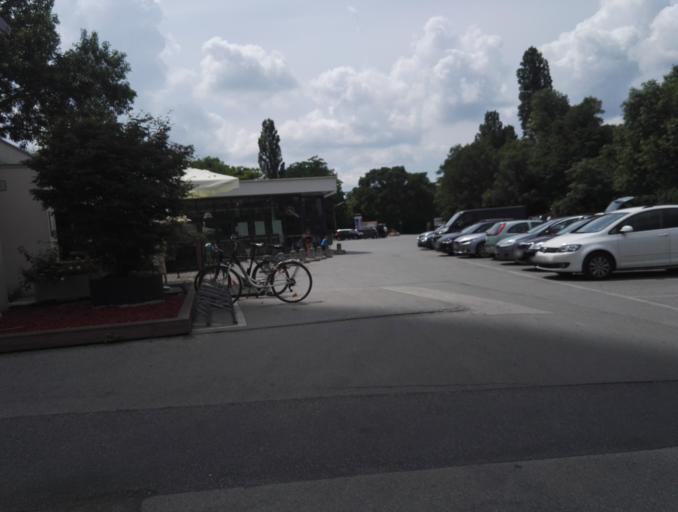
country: AT
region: Vienna
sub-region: Wien Stadt
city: Vienna
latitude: 48.2407
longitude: 16.4101
